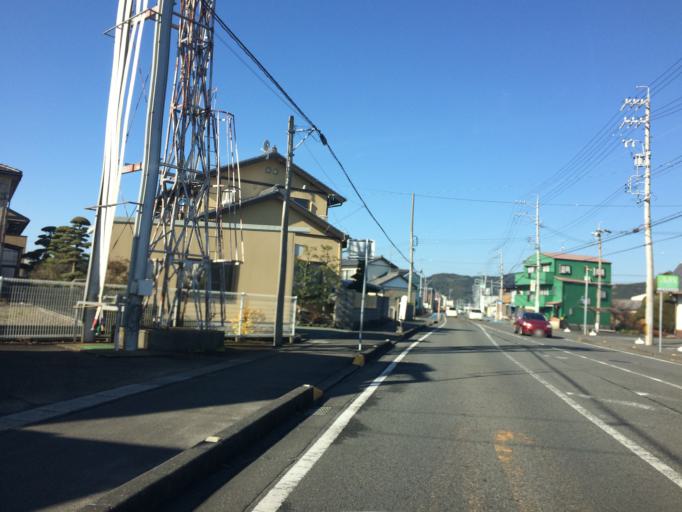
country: JP
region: Shizuoka
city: Shimada
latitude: 34.8343
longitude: 138.2173
